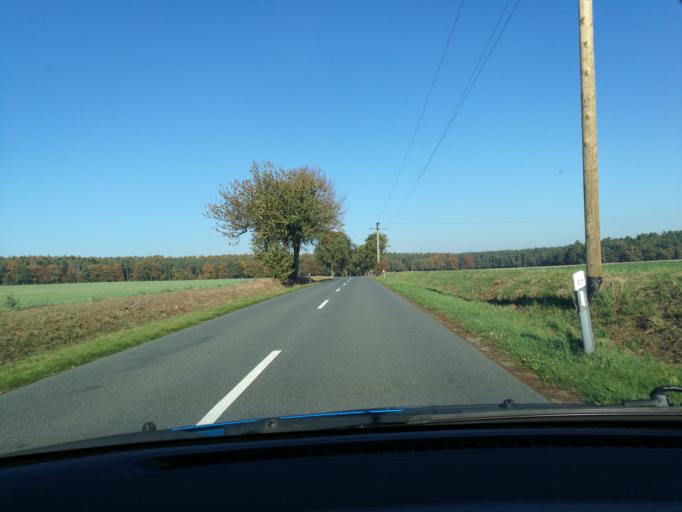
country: DE
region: Lower Saxony
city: Vastorf
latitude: 53.2082
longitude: 10.5480
